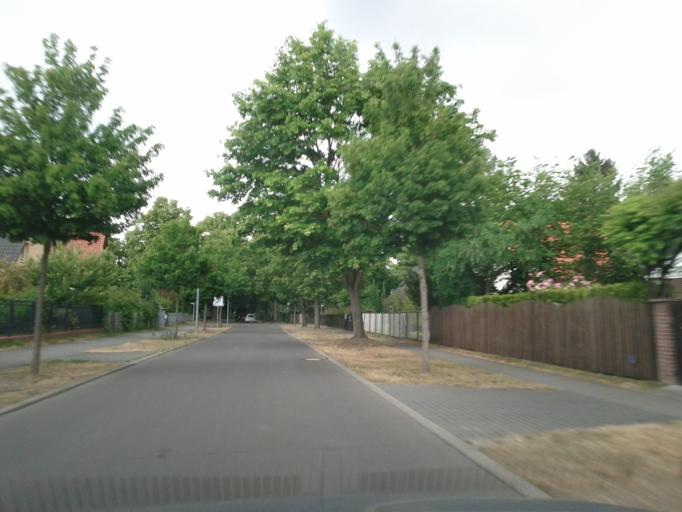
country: DE
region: Brandenburg
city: Schoneiche
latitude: 52.4707
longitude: 13.7026
